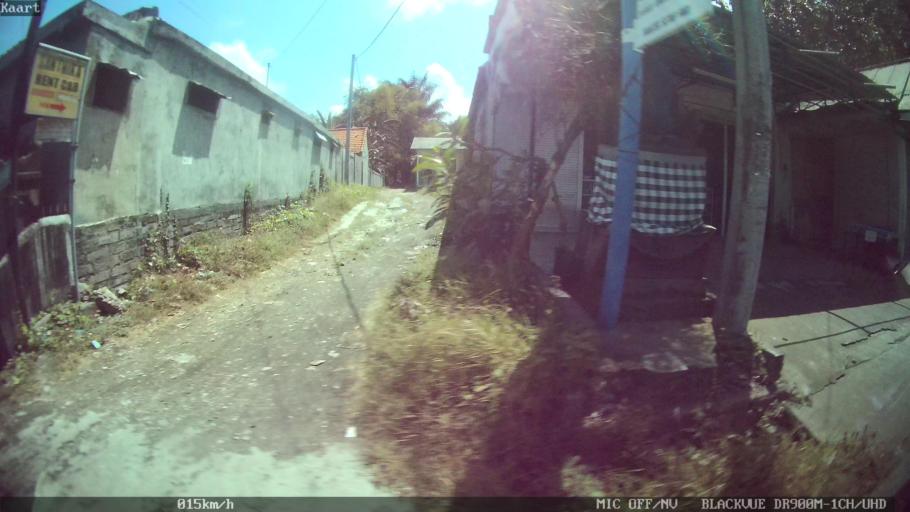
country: ID
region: Bali
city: Banjar Paangkelod
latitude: -8.6120
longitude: 115.2562
